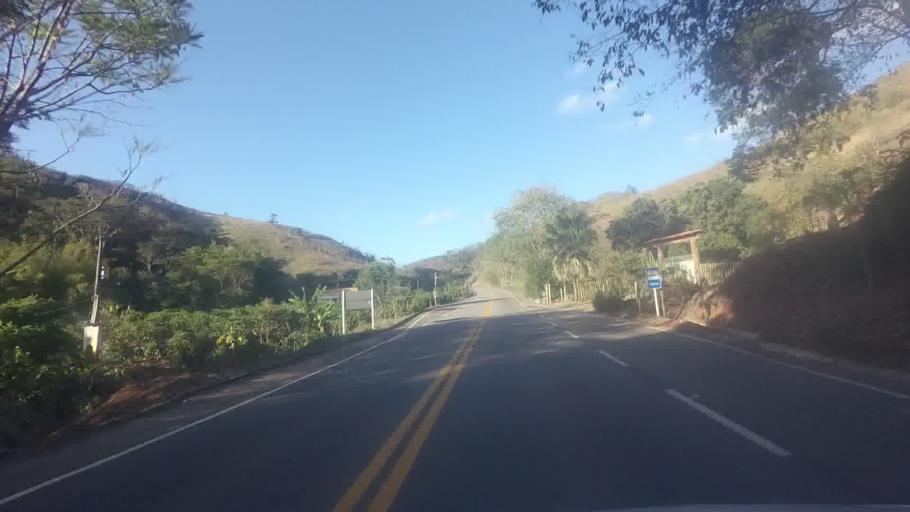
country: BR
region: Espirito Santo
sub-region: Cachoeiro De Itapemirim
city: Cachoeiro de Itapemirim
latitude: -20.8545
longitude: -41.2474
